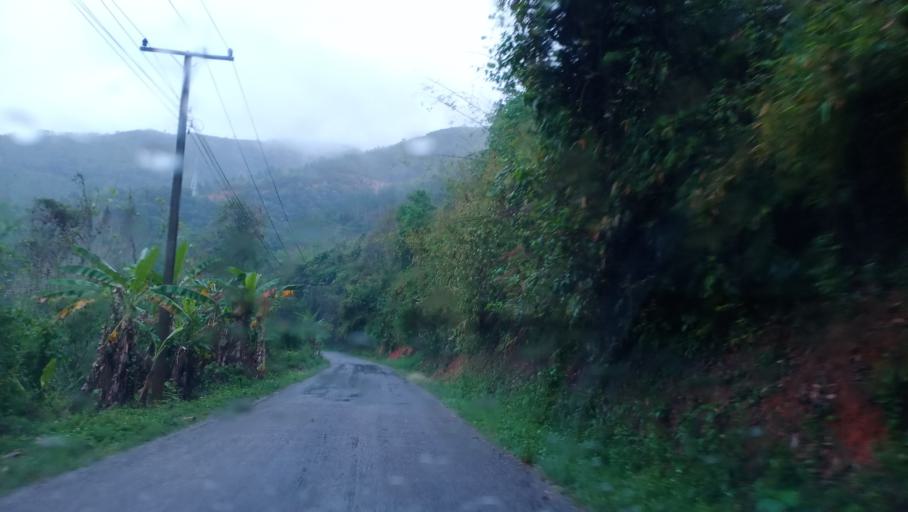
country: LA
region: Phongsali
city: Khoa
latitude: 21.0639
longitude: 102.4797
